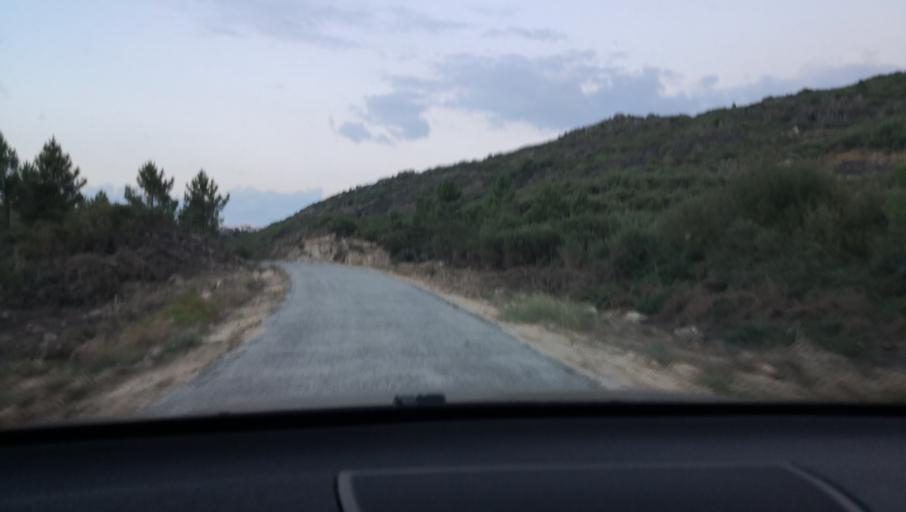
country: PT
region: Vila Real
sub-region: Sabrosa
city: Sabrosa
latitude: 41.2852
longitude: -7.6222
